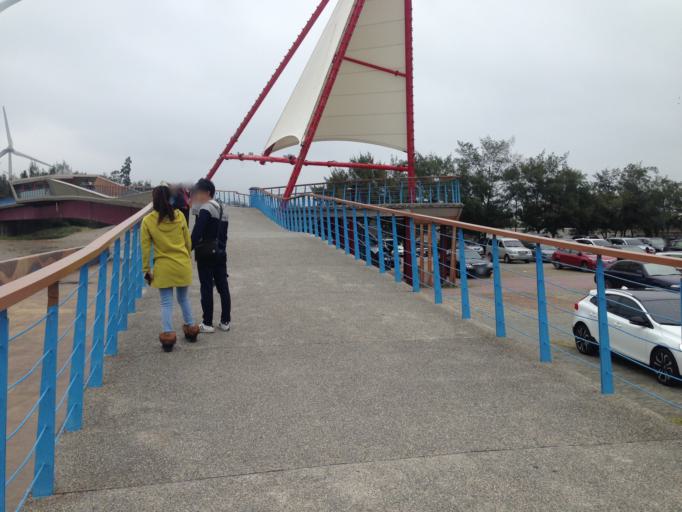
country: TW
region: Taiwan
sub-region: Miaoli
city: Miaoli
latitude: 24.7006
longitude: 120.8590
